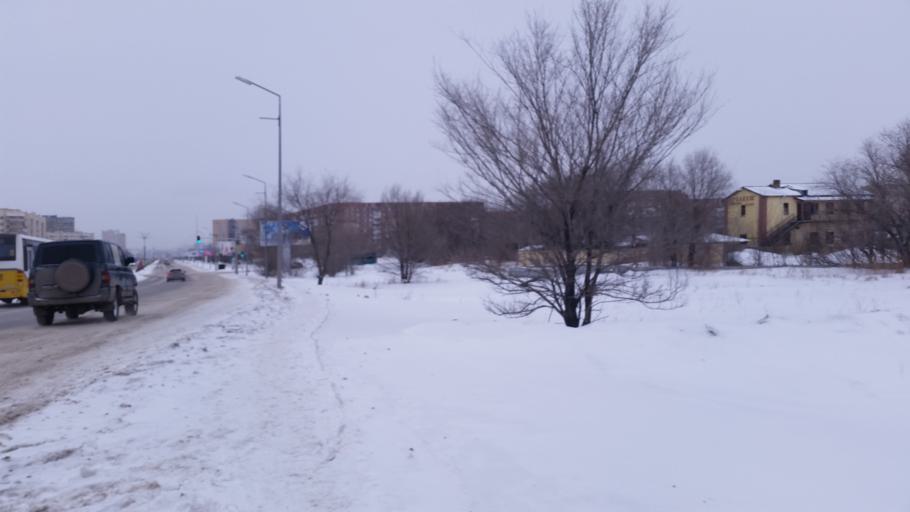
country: KZ
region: Qaraghandy
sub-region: Qaraghandy Qalasy
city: Karagandy
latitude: 49.7764
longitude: 73.1549
